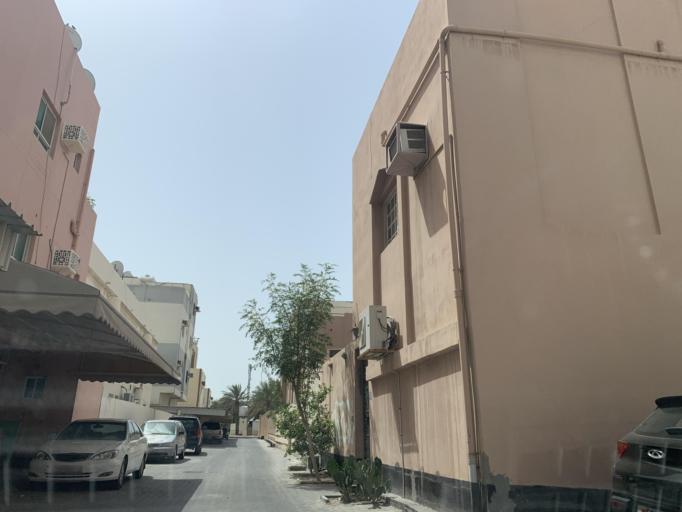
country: BH
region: Northern
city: Ar Rifa'
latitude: 26.1295
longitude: 50.5581
